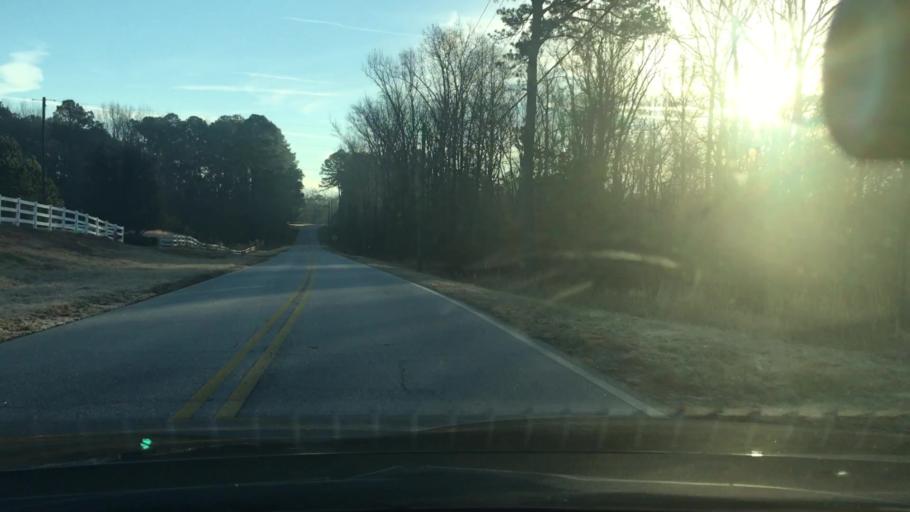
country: US
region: Georgia
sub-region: Spalding County
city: Experiment
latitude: 33.2764
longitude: -84.3704
